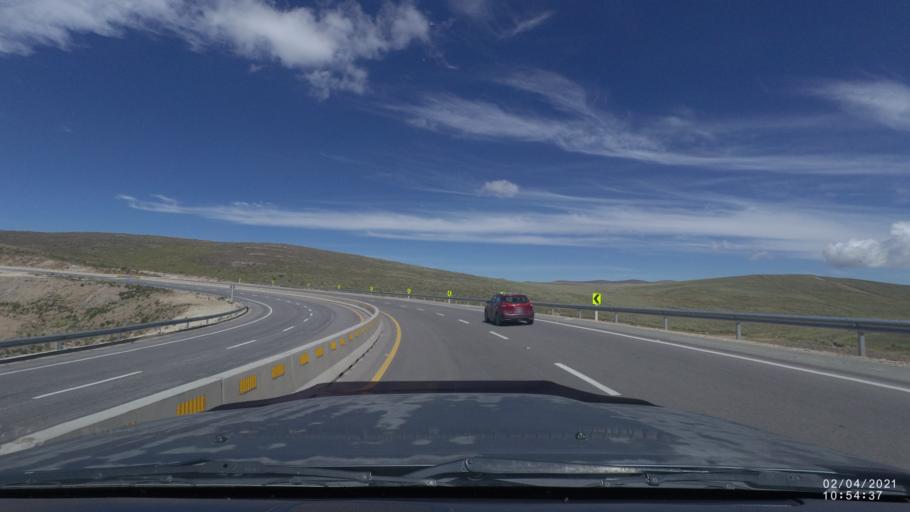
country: BO
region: Cochabamba
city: Colchani
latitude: -17.6664
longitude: -66.7581
